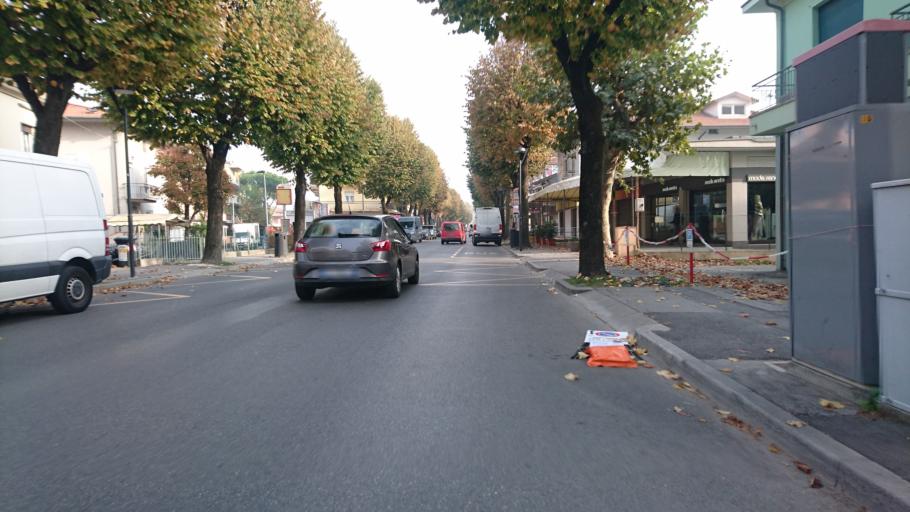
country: IT
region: Emilia-Romagna
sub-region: Provincia di Rimini
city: Rimini
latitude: 44.0760
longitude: 12.5563
